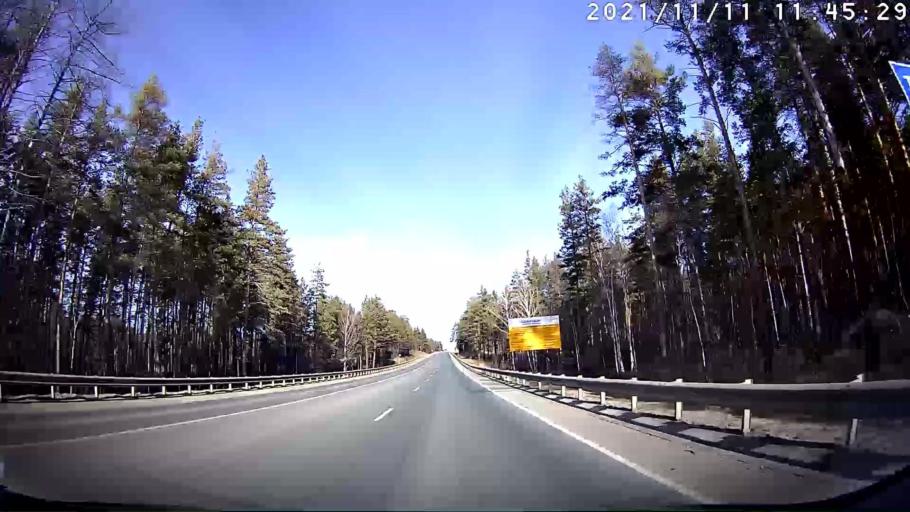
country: RU
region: Samara
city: Varlamovo
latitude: 53.4722
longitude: 48.3366
